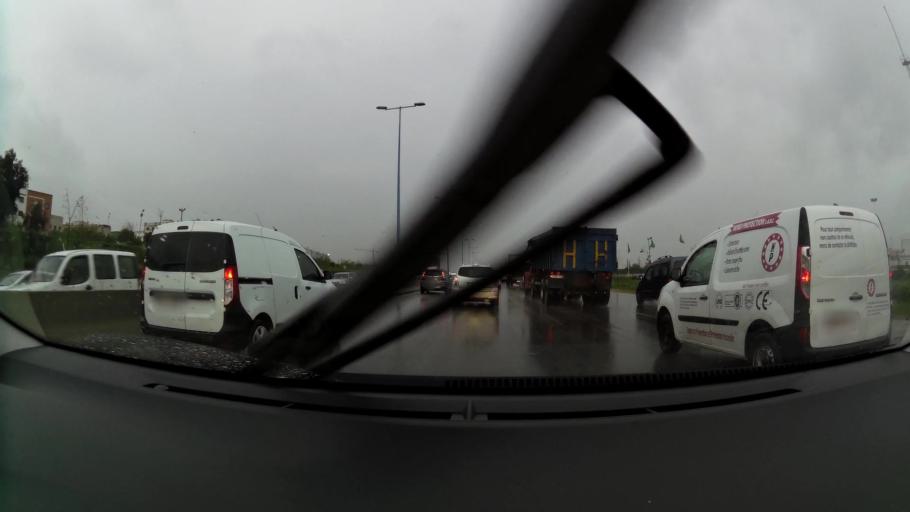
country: MA
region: Grand Casablanca
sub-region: Mediouna
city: Tit Mellil
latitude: 33.5946
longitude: -7.5209
